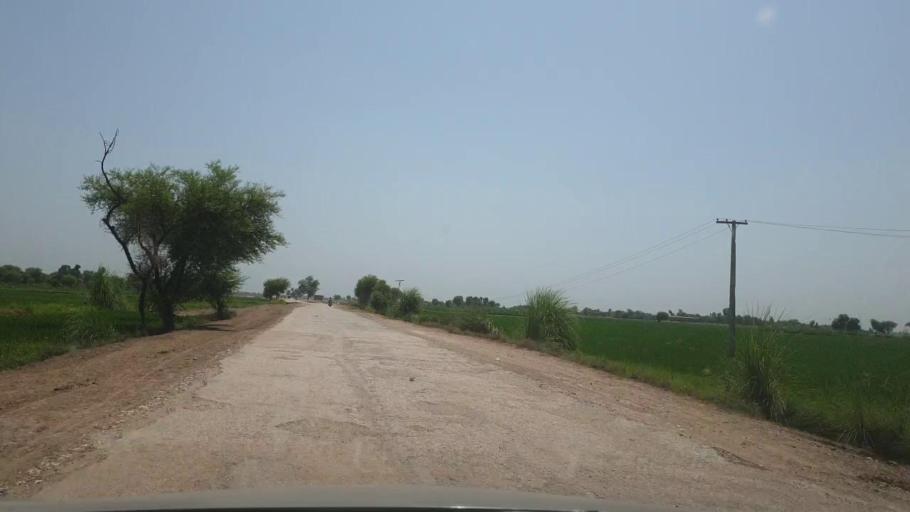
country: PK
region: Sindh
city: Warah
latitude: 27.5051
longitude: 67.7933
